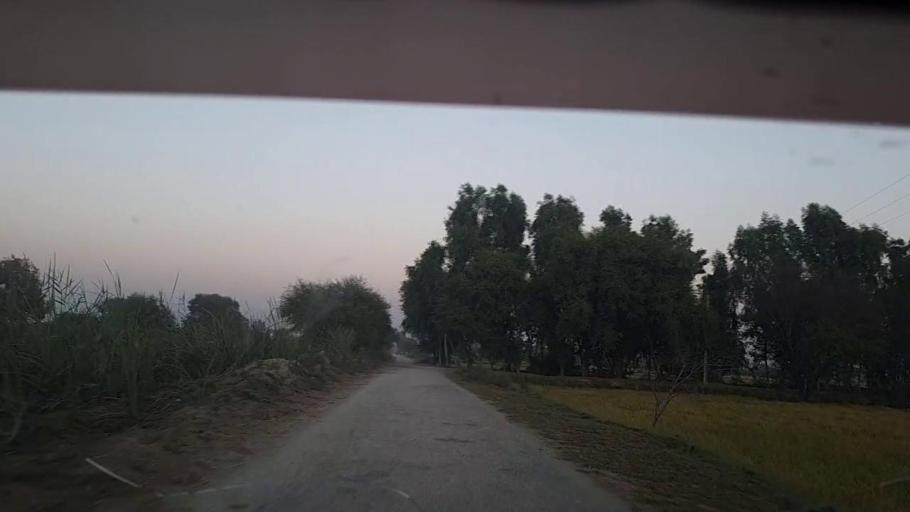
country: PK
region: Sindh
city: Ratodero
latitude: 27.8642
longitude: 68.2679
